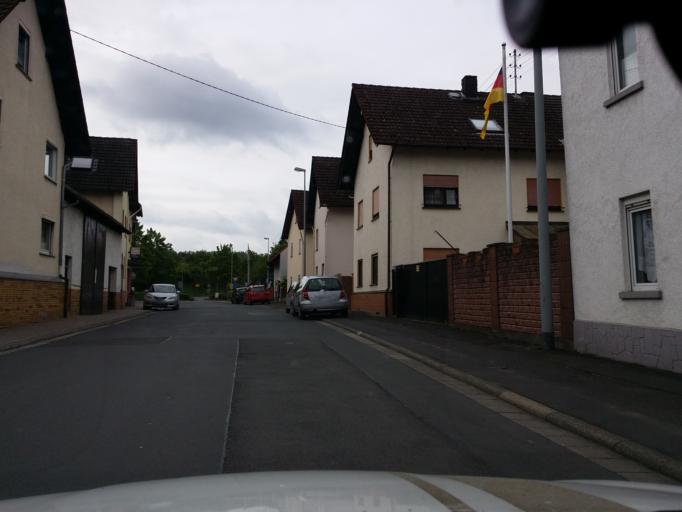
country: DE
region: Hesse
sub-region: Regierungsbezirk Darmstadt
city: Waldems
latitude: 50.2203
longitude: 8.3356
